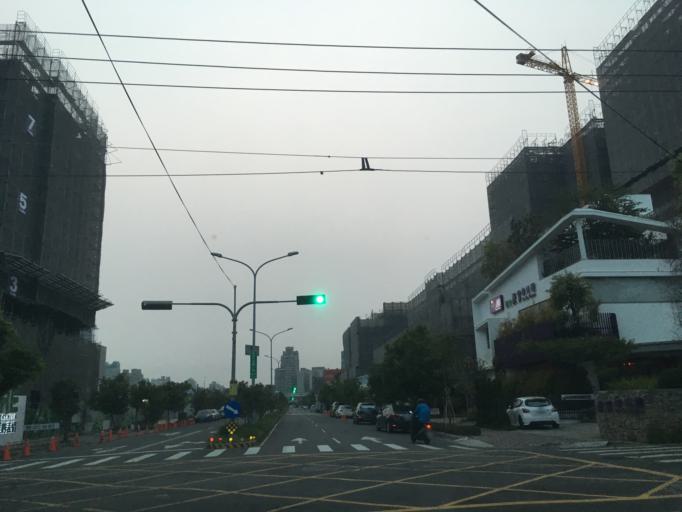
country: TW
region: Taiwan
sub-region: Taichung City
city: Taichung
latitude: 24.1747
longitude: 120.7076
